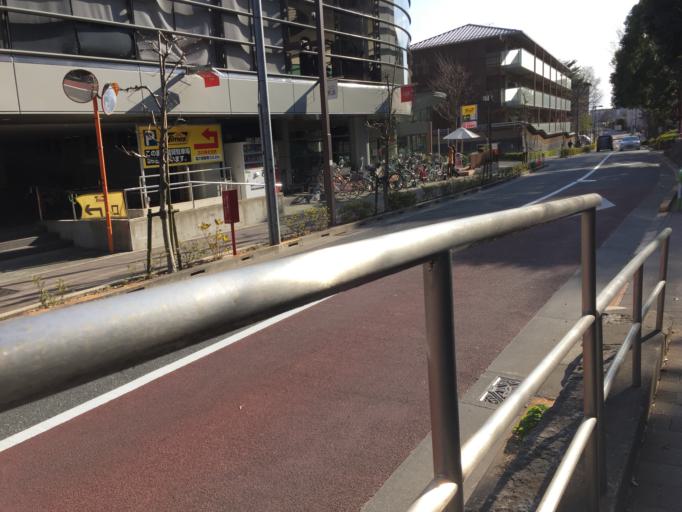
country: JP
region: Tokyo
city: Mitaka-shi
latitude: 35.6681
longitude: 139.6086
